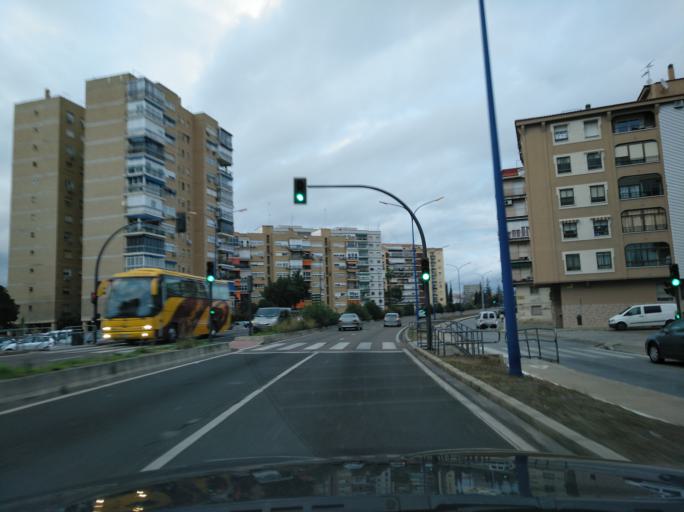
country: ES
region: Extremadura
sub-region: Provincia de Badajoz
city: Badajoz
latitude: 38.8753
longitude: -6.9813
